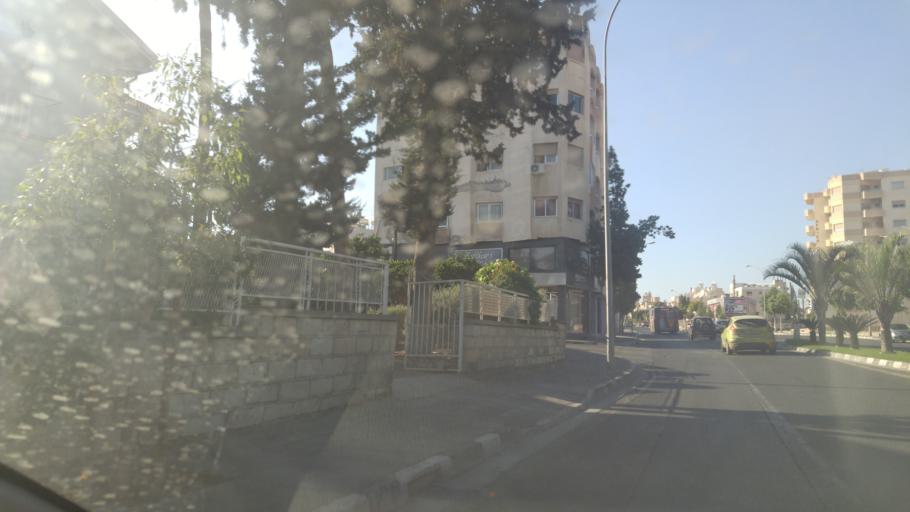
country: CY
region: Limassol
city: Limassol
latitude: 34.6838
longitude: 33.0297
